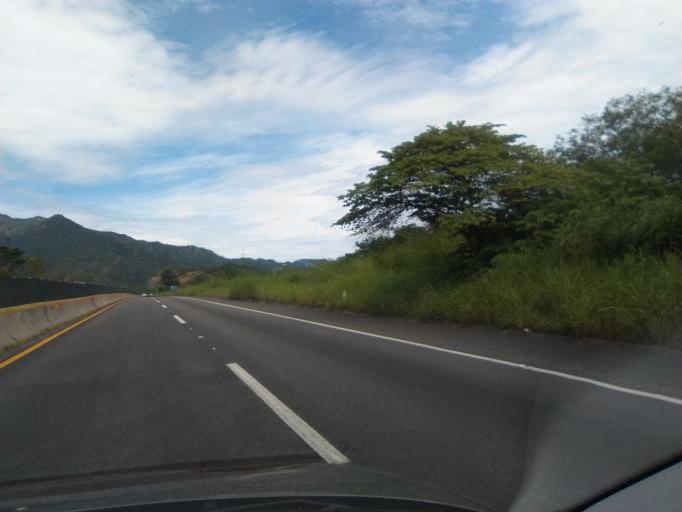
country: MX
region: Guerrero
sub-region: Chilpancingo de los Bravo
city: Cajelitos
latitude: 17.2758
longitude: -99.5092
